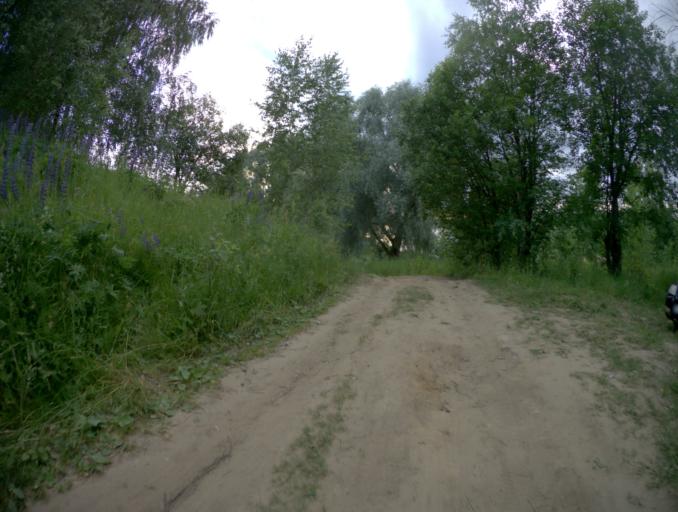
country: RU
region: Vladimir
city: Gorokhovets
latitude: 56.1920
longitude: 42.7641
